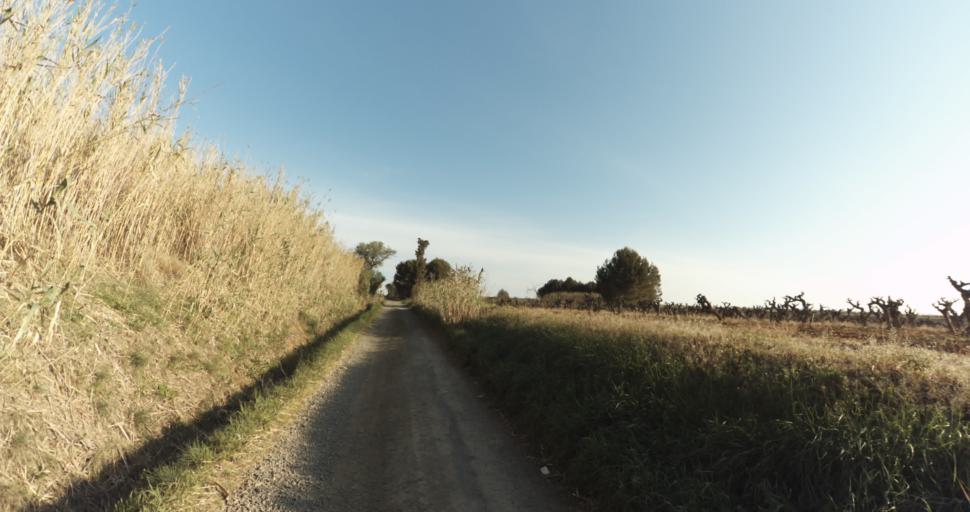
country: FR
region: Languedoc-Roussillon
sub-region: Departement de l'Herault
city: Pomerols
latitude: 43.3824
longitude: 3.5210
